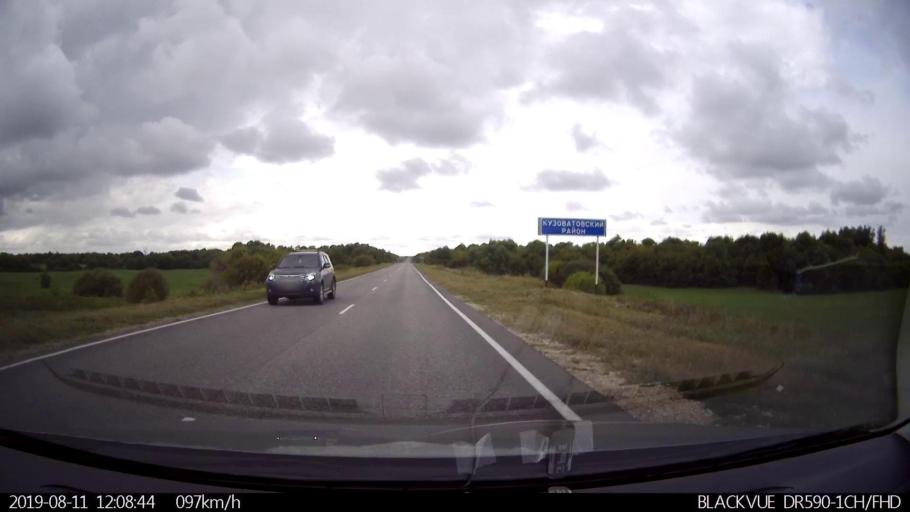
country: RU
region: Ulyanovsk
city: Silikatnyy
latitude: 53.9960
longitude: 48.0634
